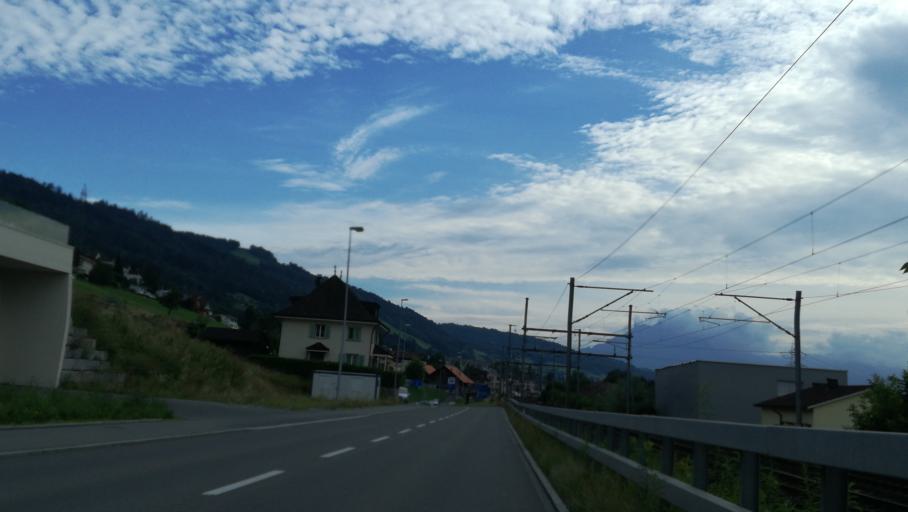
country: CH
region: Lucerne
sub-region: Lucerne-Land District
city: Root
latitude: 47.1266
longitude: 8.3988
